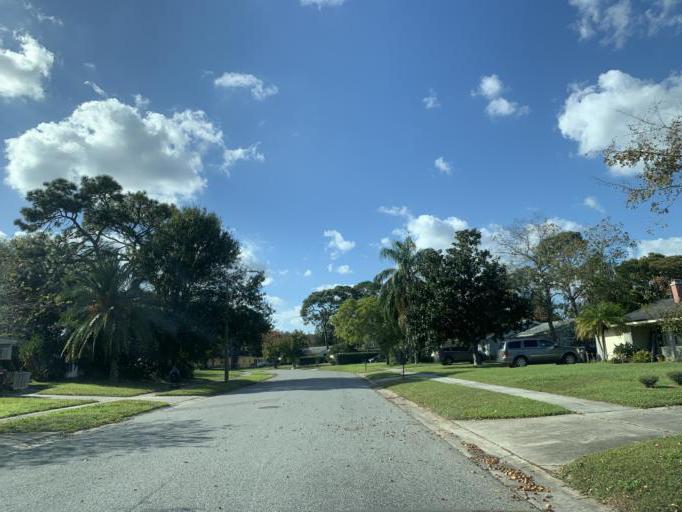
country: US
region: Florida
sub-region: Orange County
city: Eatonville
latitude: 28.6114
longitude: -81.4009
